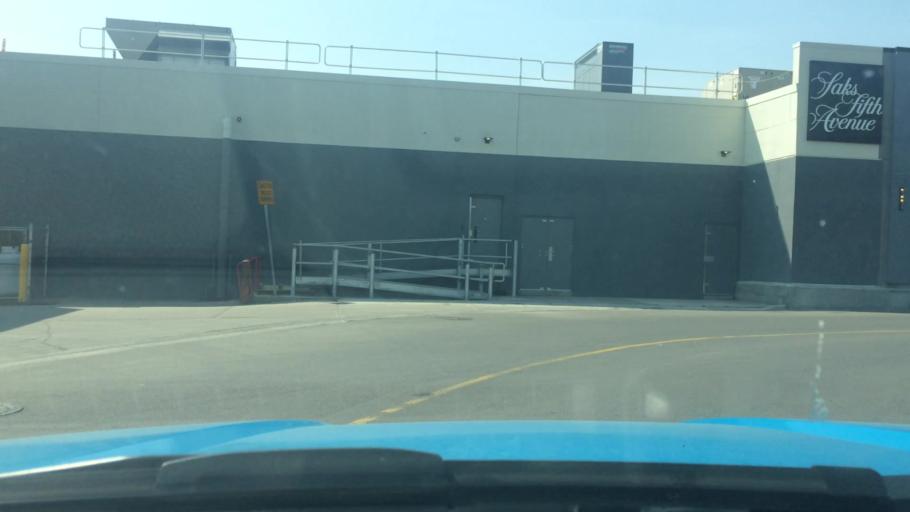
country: CA
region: Alberta
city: Calgary
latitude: 50.9997
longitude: -114.0750
